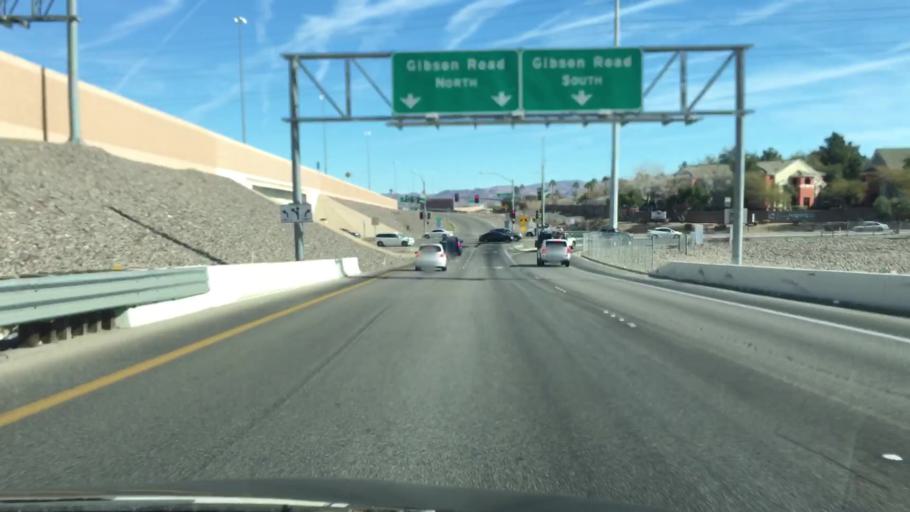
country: US
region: Nevada
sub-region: Clark County
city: Henderson
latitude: 36.0313
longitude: -115.0309
